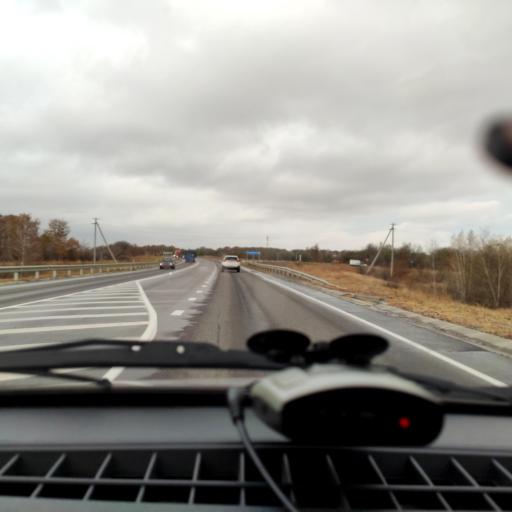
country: RU
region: Voronezj
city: Kolodeznyy
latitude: 51.3677
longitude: 39.0235
